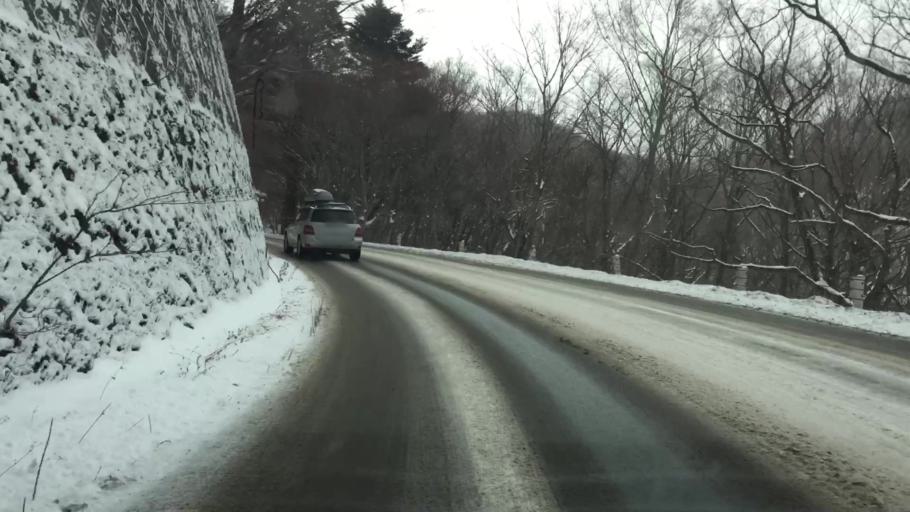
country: JP
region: Tochigi
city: Yaita
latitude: 36.9729
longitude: 139.7917
